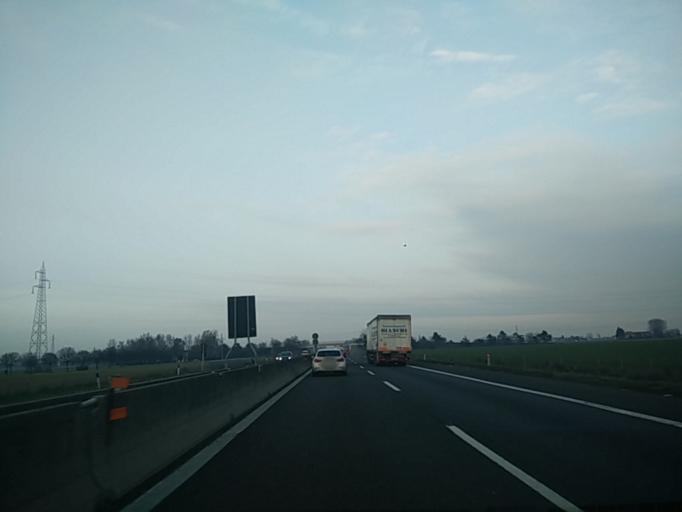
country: IT
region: Emilia-Romagna
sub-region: Provincia di Bologna
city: Progresso
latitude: 44.5725
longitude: 11.3878
